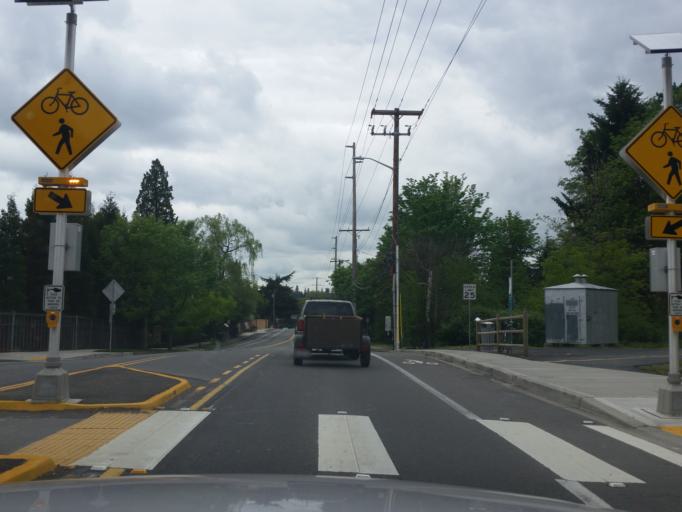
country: US
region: Washington
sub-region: King County
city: Kirkland
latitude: 47.6730
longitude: -122.1963
